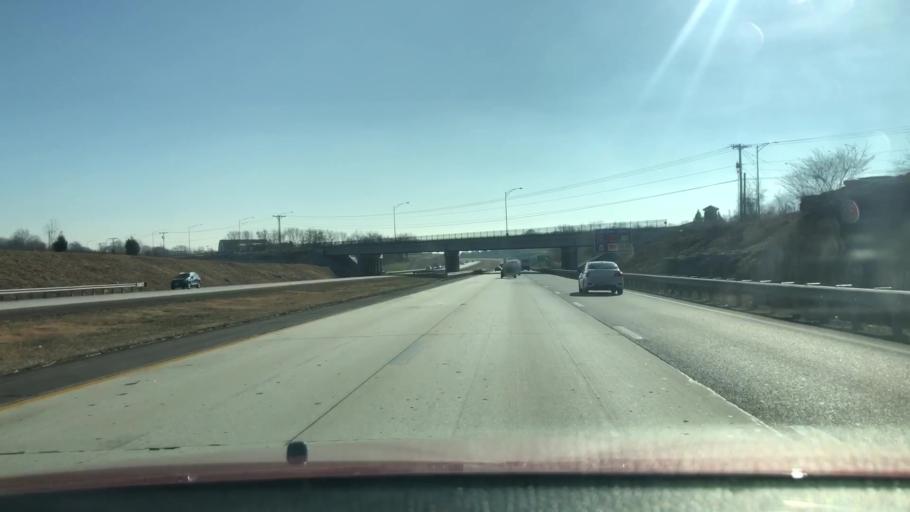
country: US
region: Missouri
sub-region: Greene County
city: Battlefield
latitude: 37.1393
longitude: -93.3126
